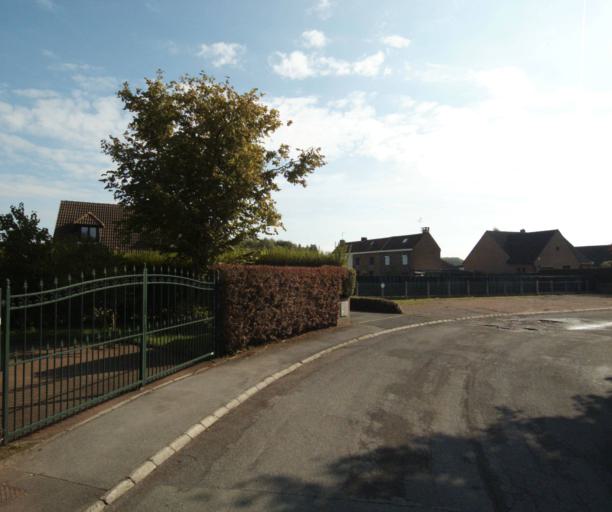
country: FR
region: Nord-Pas-de-Calais
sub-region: Departement du Nord
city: Lompret
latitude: 50.6739
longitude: 2.9868
